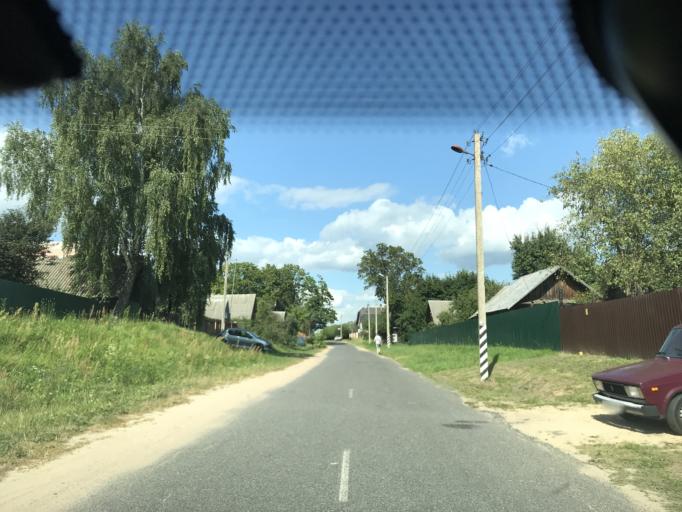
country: BY
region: Mogilev
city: Poselok Voskhod
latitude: 53.7891
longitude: 30.3582
